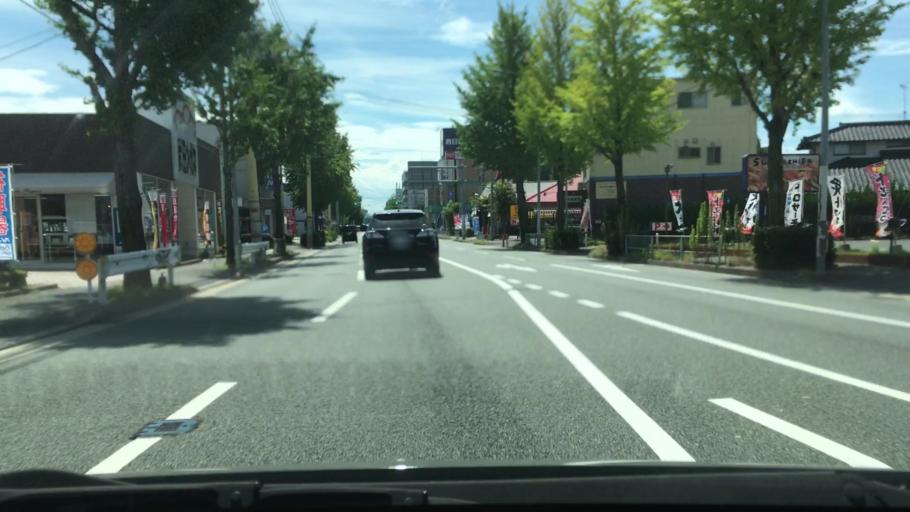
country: JP
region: Fukuoka
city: Onojo
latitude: 33.5603
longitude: 130.4486
